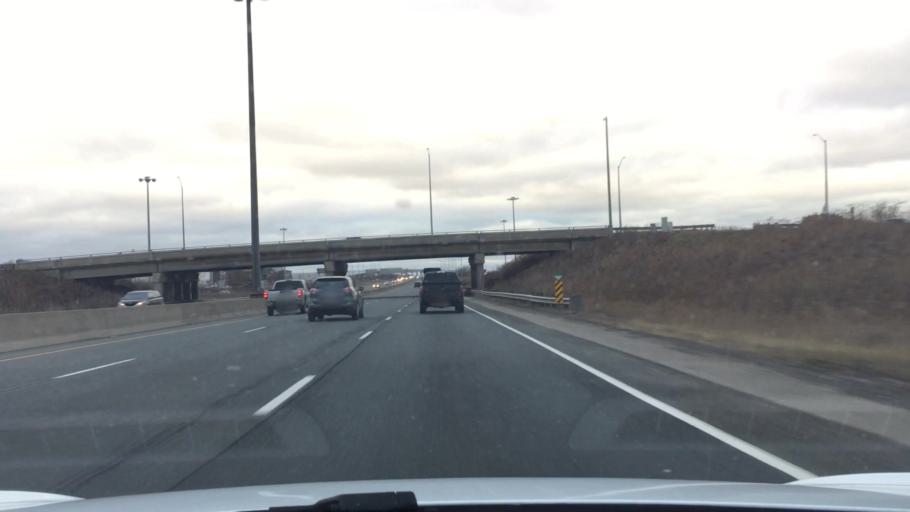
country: CA
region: Ontario
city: Thorold
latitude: 43.1568
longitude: -79.1633
